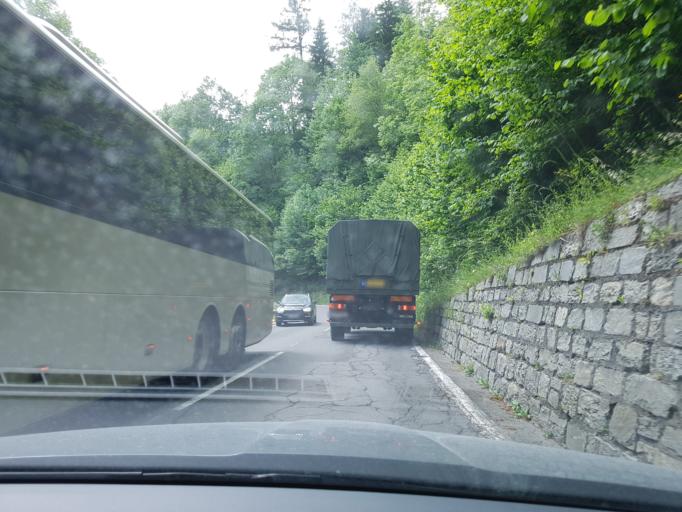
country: AT
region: Carinthia
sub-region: Politischer Bezirk Villach Land
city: Feld am See
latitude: 46.7977
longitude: 13.7460
